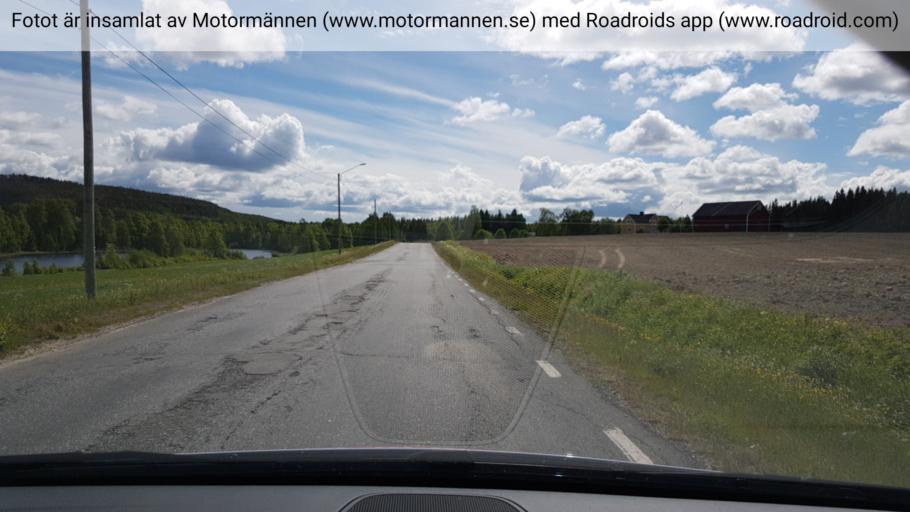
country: SE
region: Vaesterbotten
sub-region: Vannas Kommun
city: Vannasby
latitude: 64.0756
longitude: 19.9694
